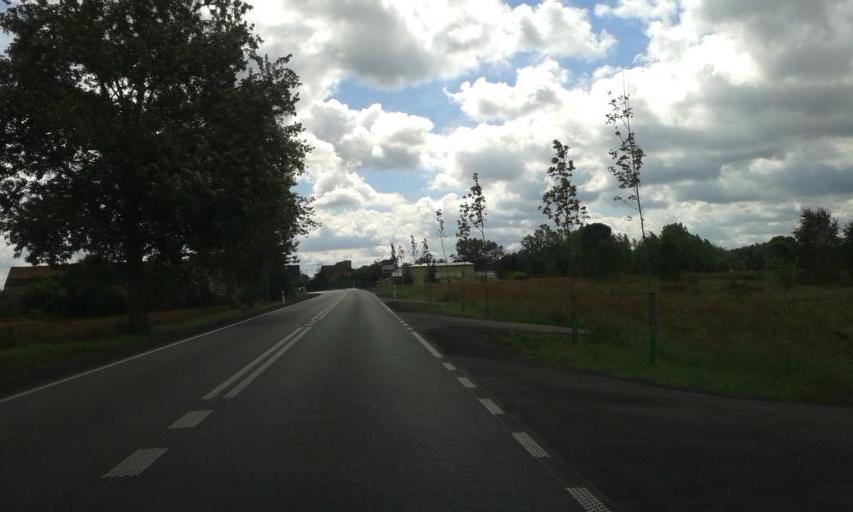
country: PL
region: West Pomeranian Voivodeship
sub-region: Powiat drawski
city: Czaplinek
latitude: 53.5293
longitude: 16.2989
